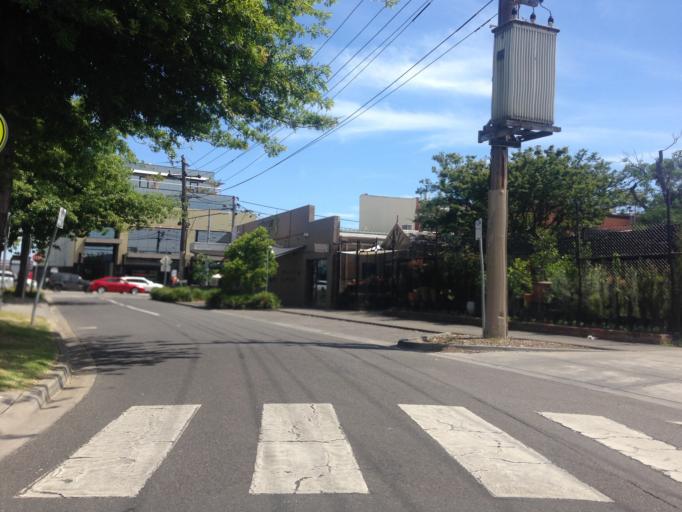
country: AU
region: Victoria
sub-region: Boroondara
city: Kew East
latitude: -37.7923
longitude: 145.0722
